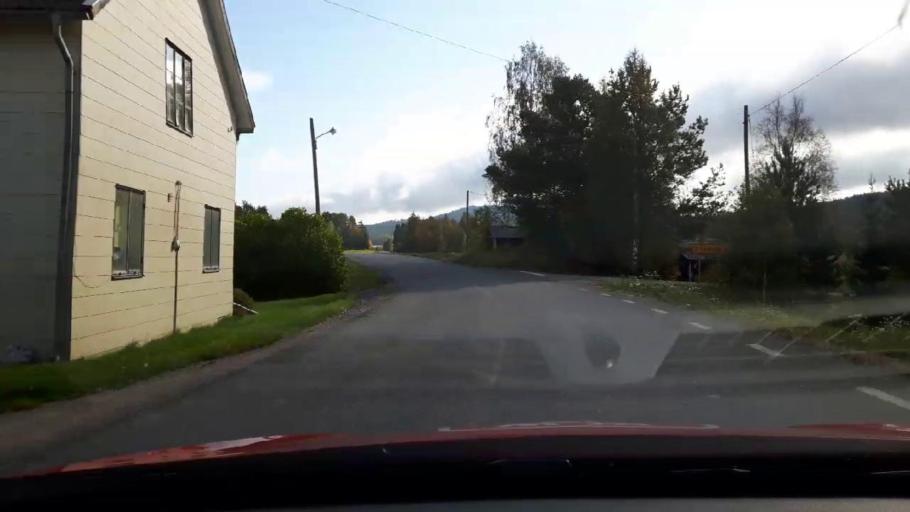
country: SE
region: Gaevleborg
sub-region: Ljusdals Kommun
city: Farila
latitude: 61.7706
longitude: 15.9670
